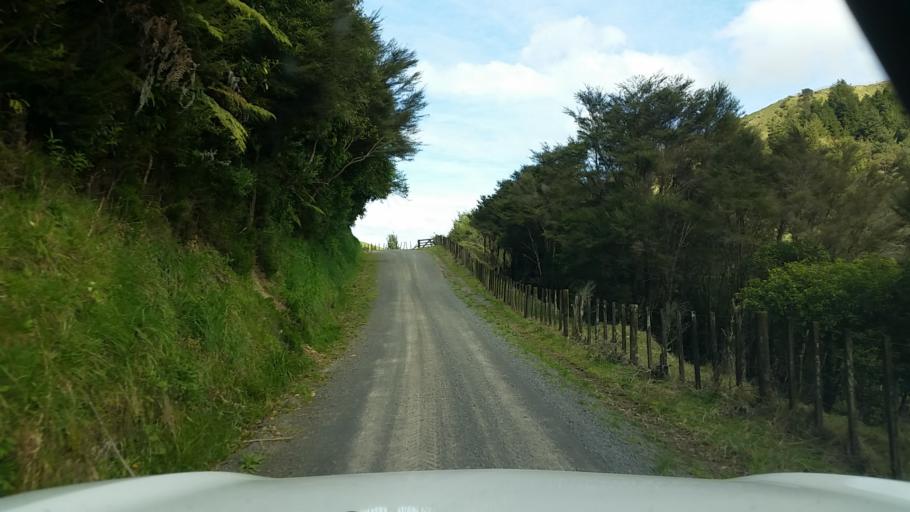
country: NZ
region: Waikato
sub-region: Hauraki District
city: Ngatea
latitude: -37.4722
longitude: 175.4569
